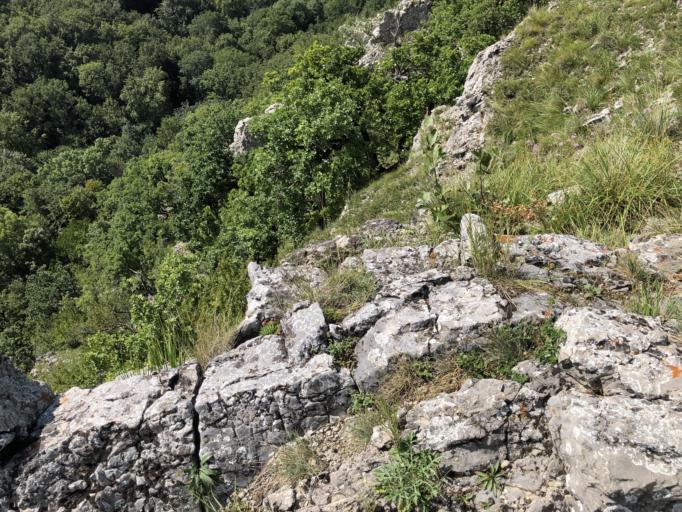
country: HU
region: Heves
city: Szilvasvarad
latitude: 48.1351
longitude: 20.5185
